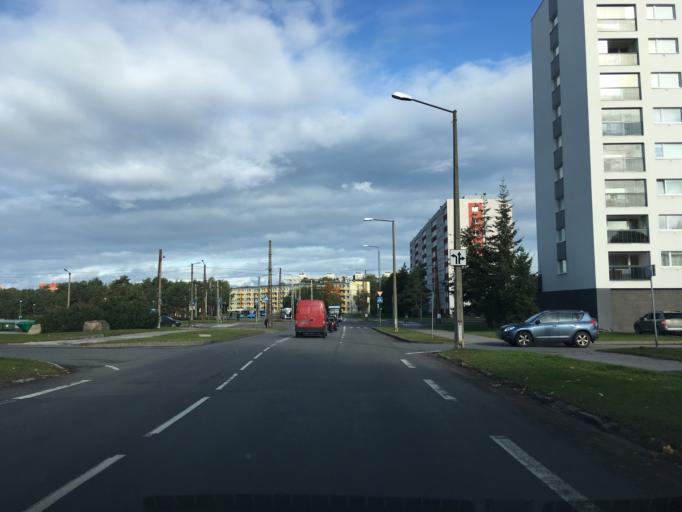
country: EE
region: Harju
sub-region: Tallinna linn
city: Tallinn
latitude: 59.3979
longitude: 24.6816
